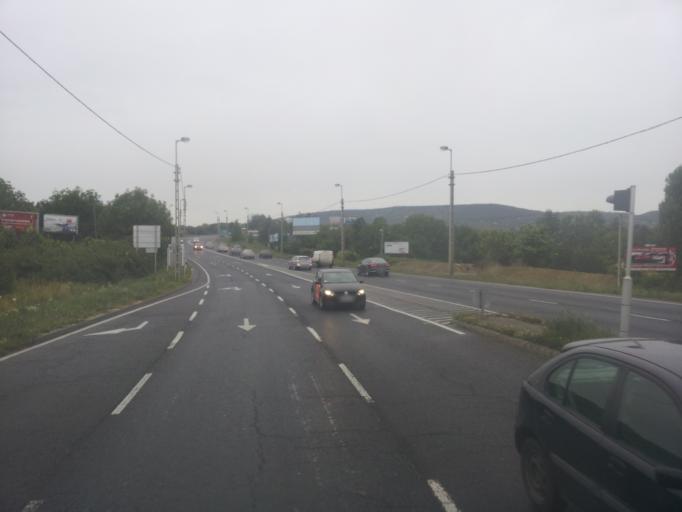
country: HU
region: Pest
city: Budaors
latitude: 47.4564
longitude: 18.9936
